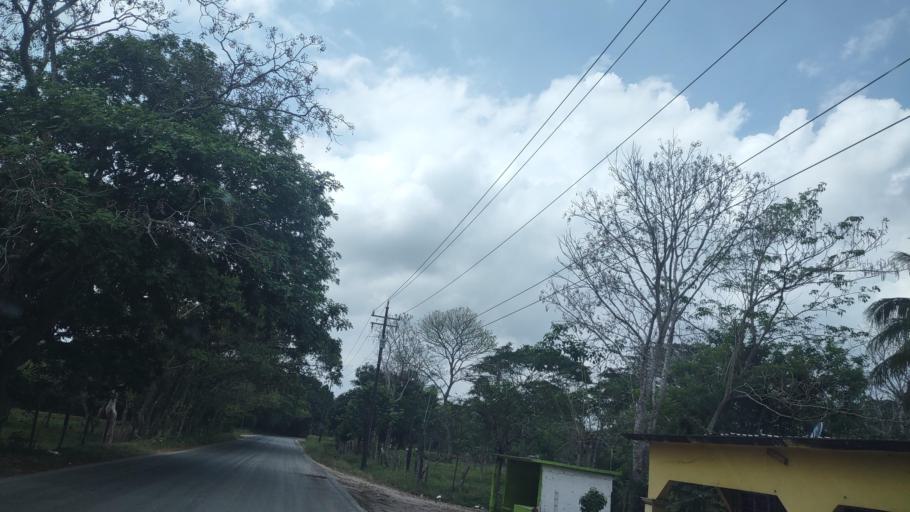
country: MX
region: Veracruz
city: Las Choapas
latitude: 17.9650
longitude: -94.1109
